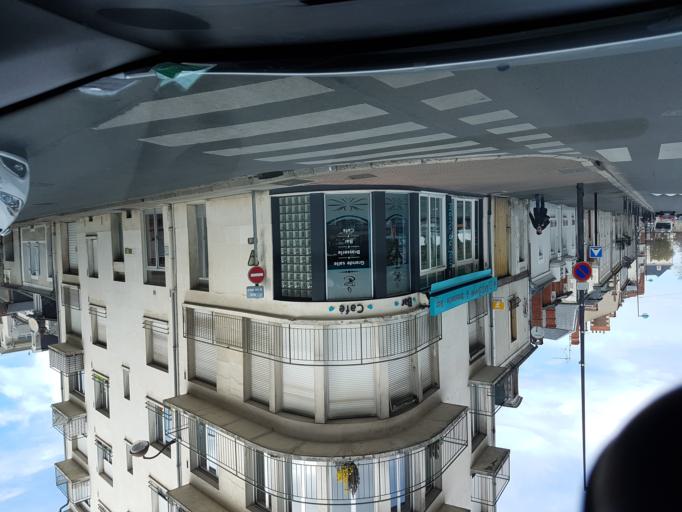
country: FR
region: Centre
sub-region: Departement du Cher
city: Bourges
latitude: 47.0776
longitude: 2.4000
